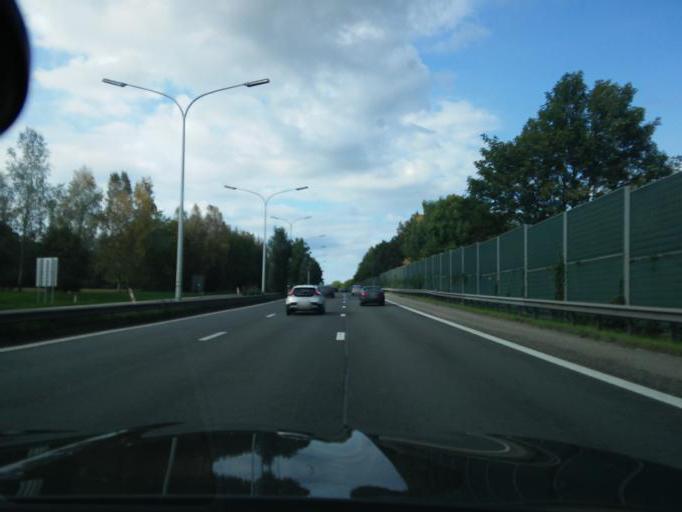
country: BE
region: Flanders
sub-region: Provincie Vlaams-Brabant
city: Meise
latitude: 50.9218
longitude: 4.3395
